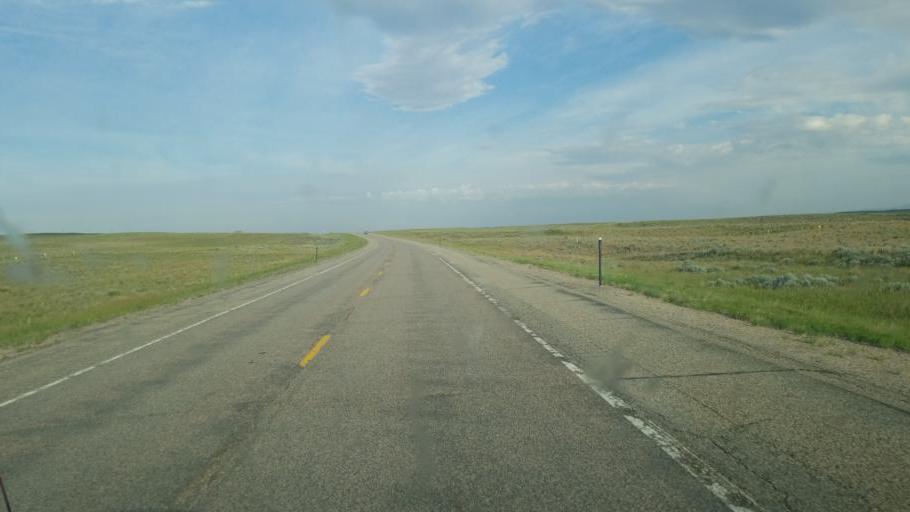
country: US
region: Wyoming
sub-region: Natrona County
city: Bar Nunn
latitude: 43.0345
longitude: -106.8563
